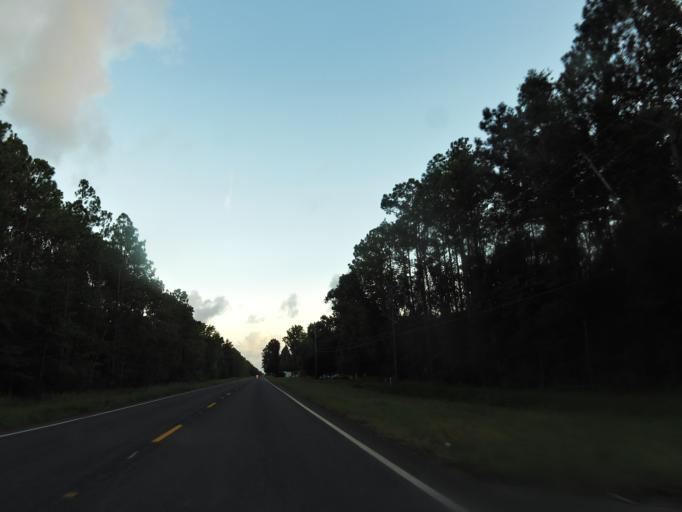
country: US
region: Georgia
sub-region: Camden County
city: Woodbine
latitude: 30.9167
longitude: -81.7133
